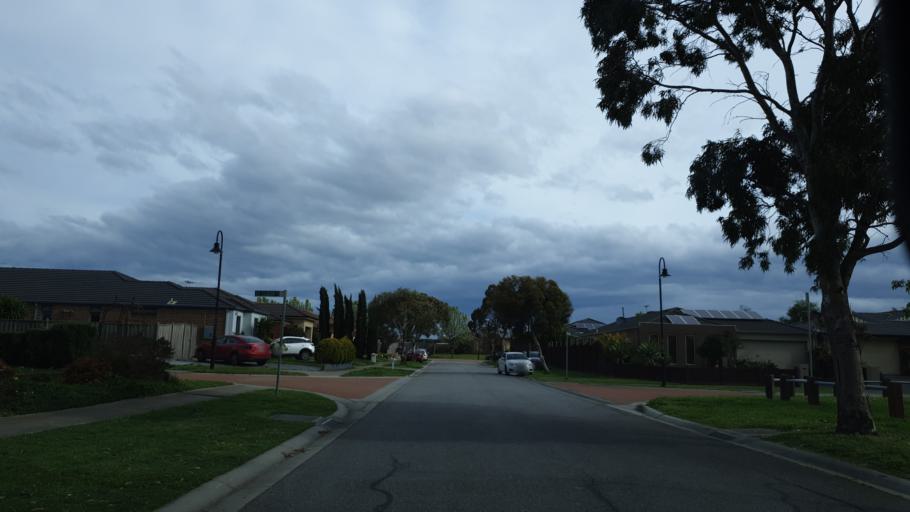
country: AU
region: Victoria
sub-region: Casey
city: Cranbourne North
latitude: -38.0726
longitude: 145.2934
